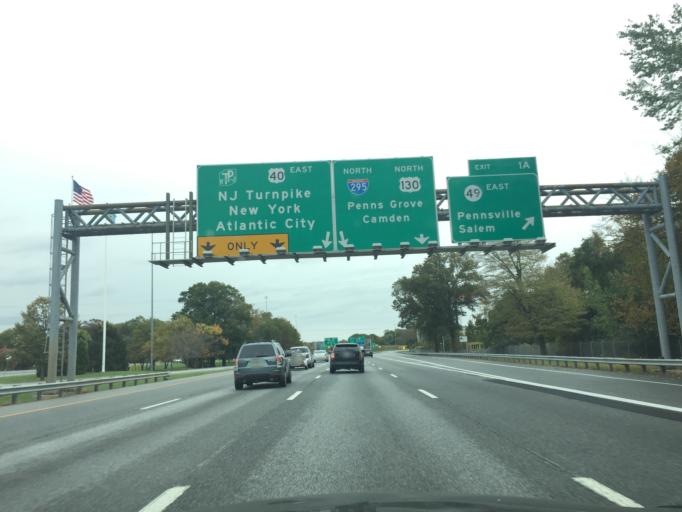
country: US
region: New Jersey
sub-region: Salem County
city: Pennsville
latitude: 39.6819
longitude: -75.4992
